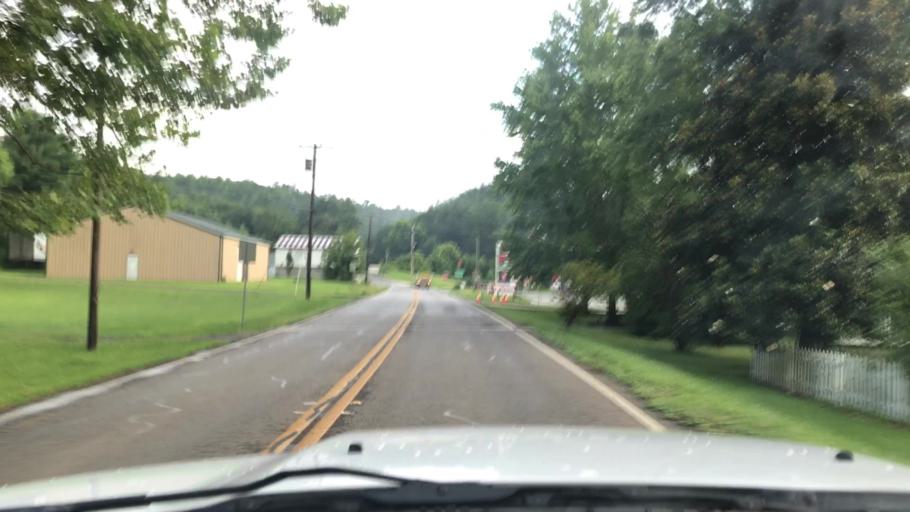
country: US
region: Georgia
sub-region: Fannin County
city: Blue Ridge
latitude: 34.9160
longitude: -84.2764
